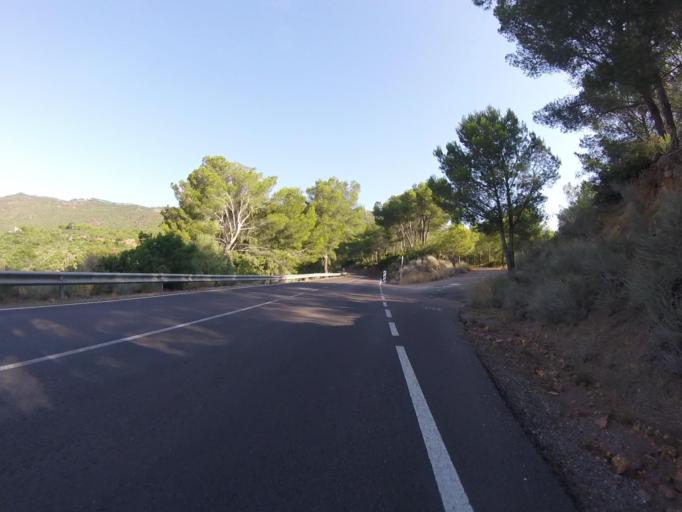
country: ES
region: Valencia
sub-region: Provincia de Castello
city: Benicassim
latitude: 40.0772
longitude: 0.0440
